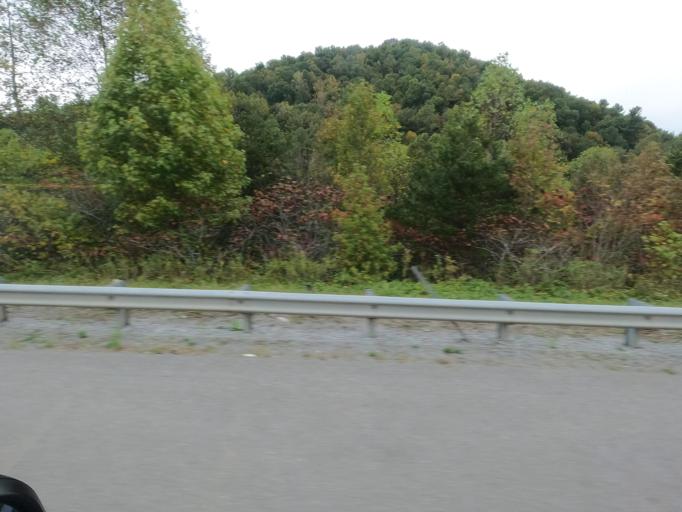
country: US
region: Tennessee
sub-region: Unicoi County
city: Erwin
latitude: 36.1711
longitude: -82.3922
